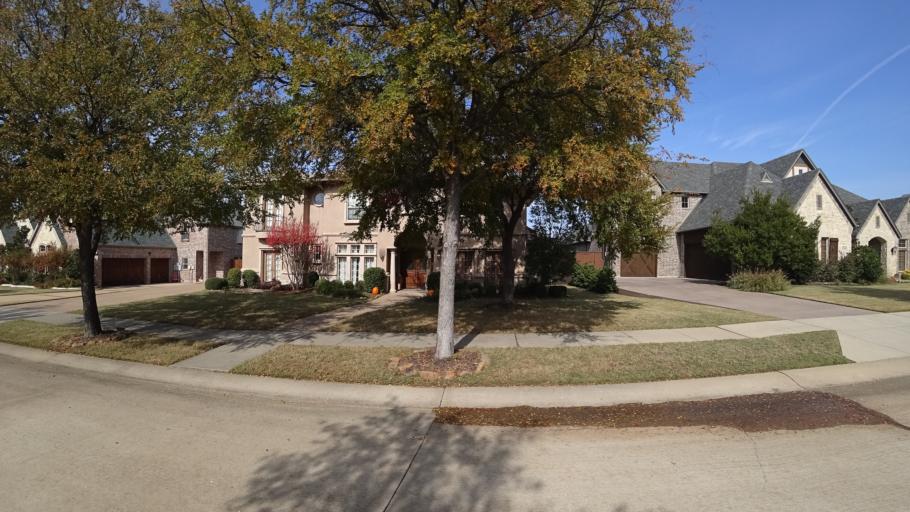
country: US
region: Texas
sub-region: Denton County
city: The Colony
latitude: 33.0407
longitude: -96.8952
